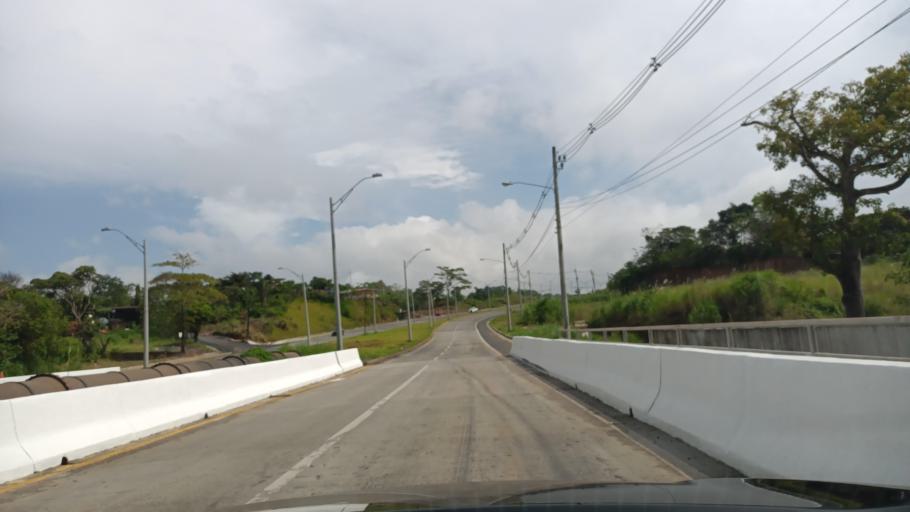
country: PA
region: Panama
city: Las Cumbres
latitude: 9.0989
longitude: -79.5048
